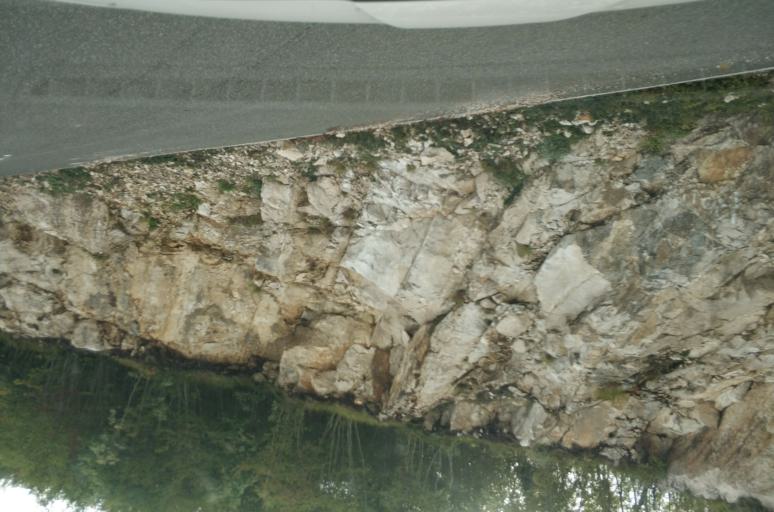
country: AL
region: Durres
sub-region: Rrethi i Krujes
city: Kruje
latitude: 41.5242
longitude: 19.8086
